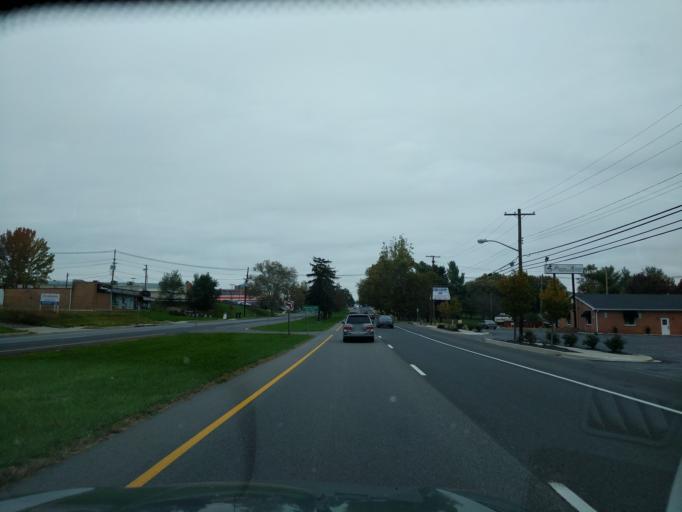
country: US
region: Maryland
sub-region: Washington County
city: Hagerstown
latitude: 39.6349
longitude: -77.7047
